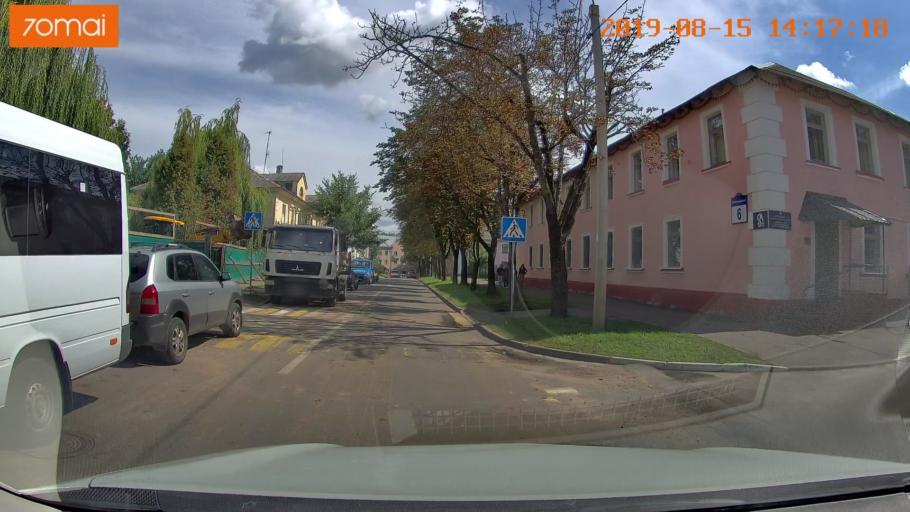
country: BY
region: Minsk
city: Minsk
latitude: 53.8844
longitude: 27.5957
